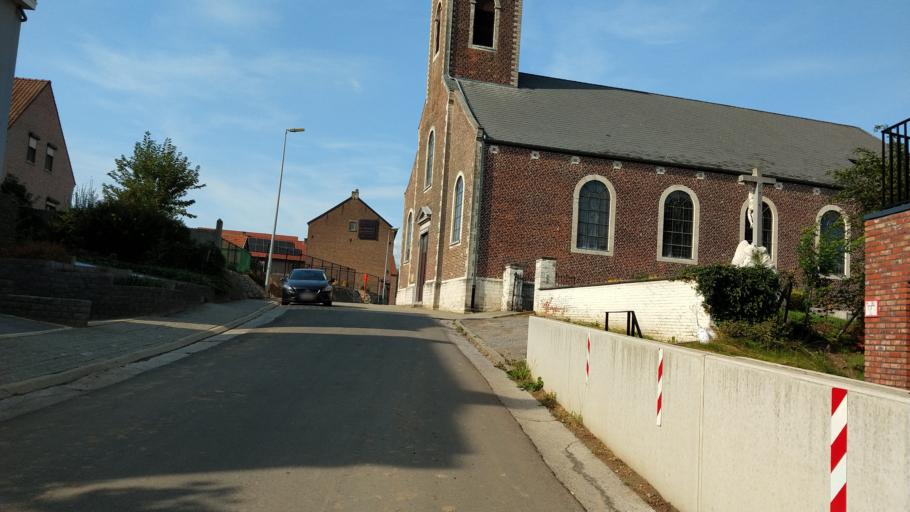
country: BE
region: Flanders
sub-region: Provincie Vlaams-Brabant
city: Boutersem
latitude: 50.8384
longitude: 4.8319
